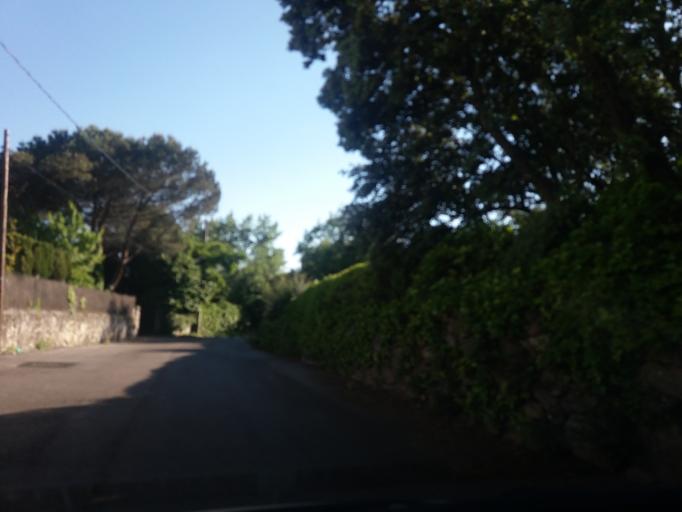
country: ES
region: Madrid
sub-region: Provincia de Madrid
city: Torrelodones
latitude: 40.5862
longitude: -3.9553
